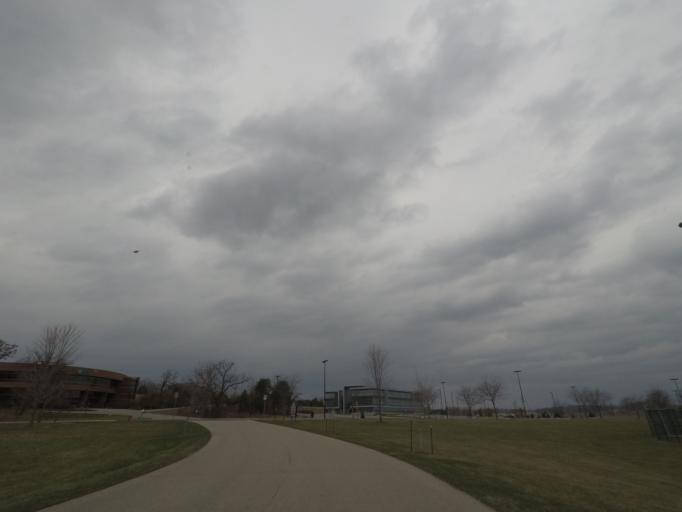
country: US
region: Wisconsin
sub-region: Dane County
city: Middleton
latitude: 43.1095
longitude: -89.5370
